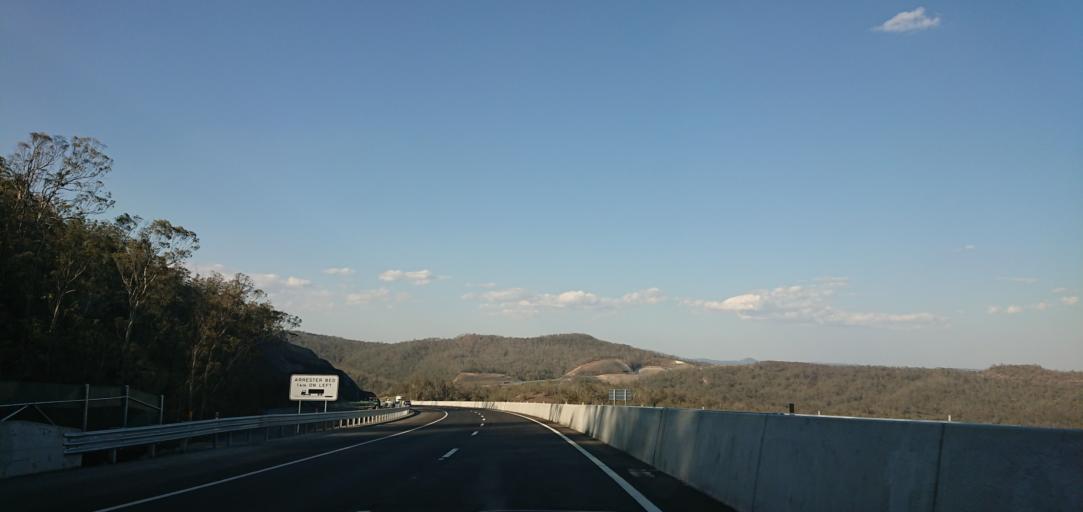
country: AU
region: Queensland
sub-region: Toowoomba
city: Wilsonton Heights
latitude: -27.5113
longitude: 151.9661
